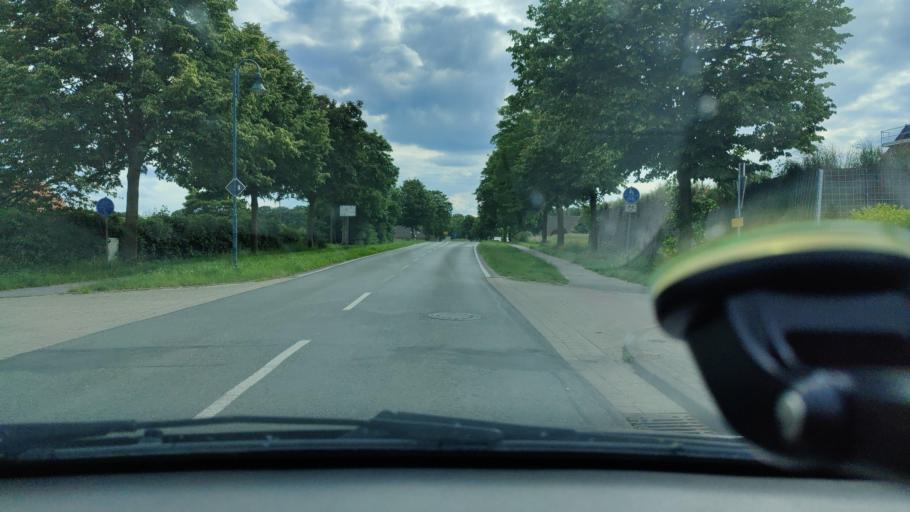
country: DE
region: North Rhine-Westphalia
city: Kalkar
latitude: 51.7348
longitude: 6.2834
